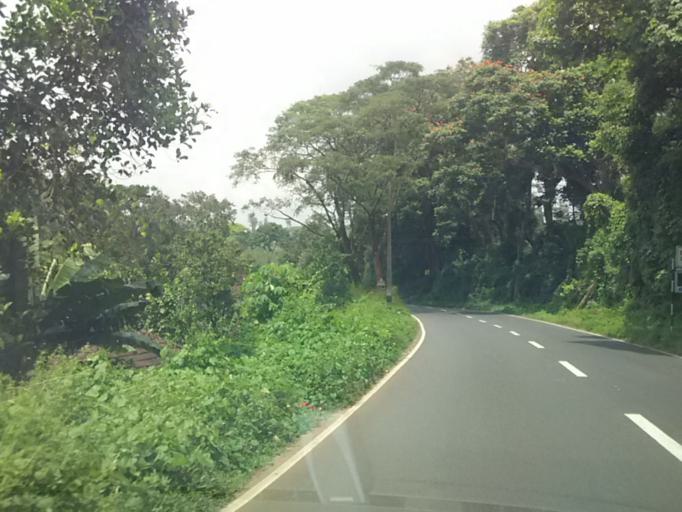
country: IN
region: Kerala
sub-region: Wayanad
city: Kalpetta
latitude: 11.5662
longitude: 76.0433
